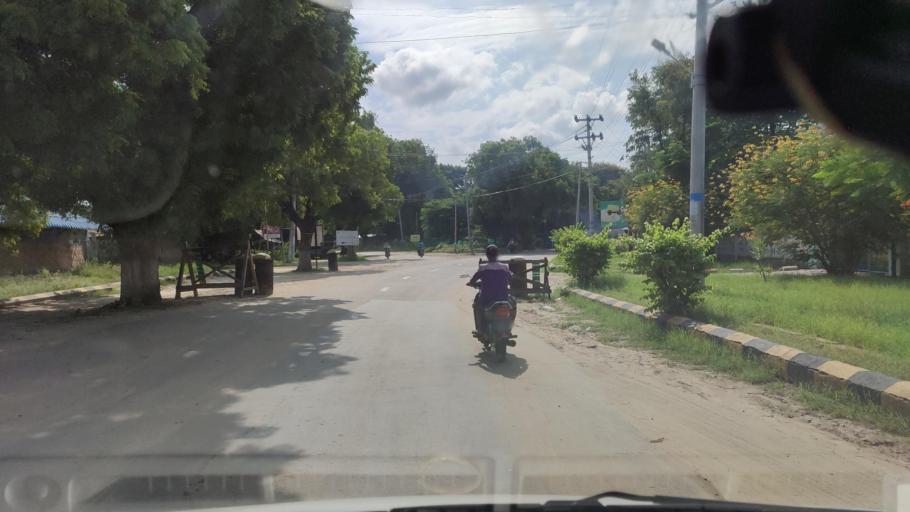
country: MM
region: Mandalay
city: Meiktila
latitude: 21.0999
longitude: 95.6497
